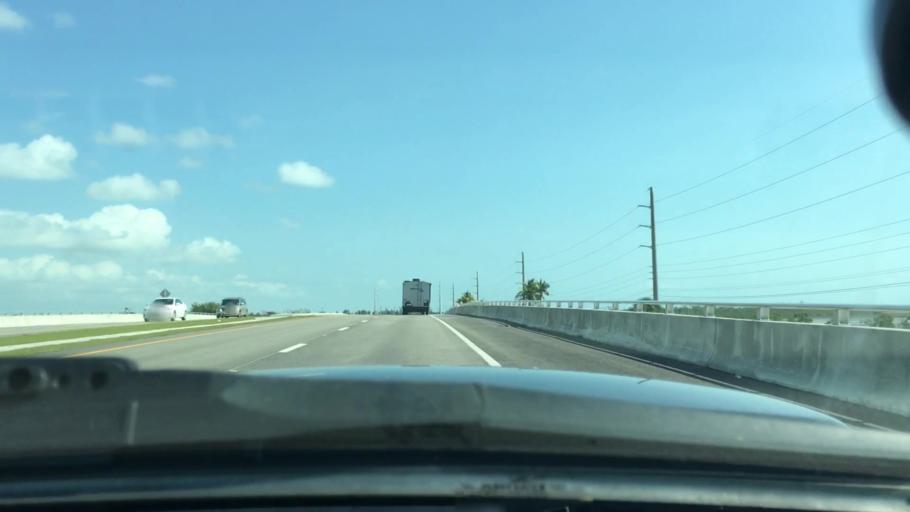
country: US
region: Florida
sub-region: Monroe County
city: Big Coppitt Key
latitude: 24.5879
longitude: -81.6916
